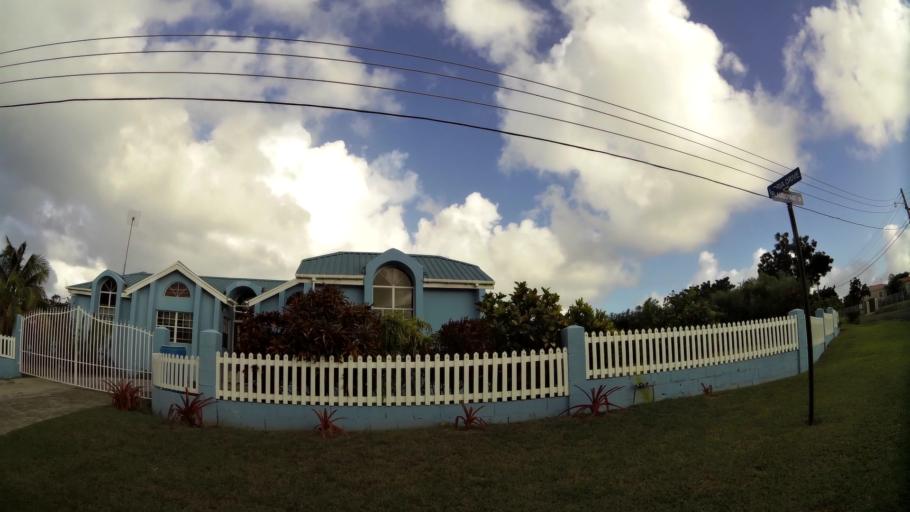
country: AG
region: Saint George
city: Piggotts
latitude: 17.1637
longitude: -61.8125
